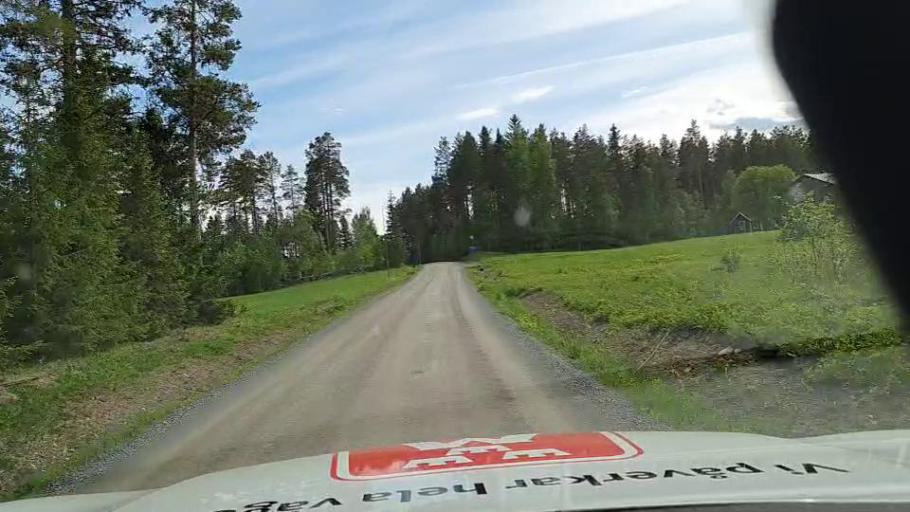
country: SE
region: Jaemtland
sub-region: OEstersunds Kommun
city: Brunflo
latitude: 62.9944
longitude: 14.8072
